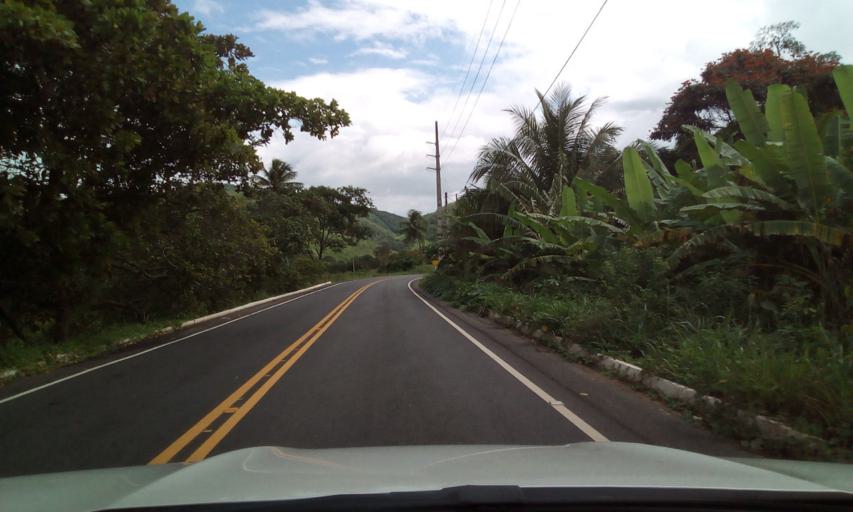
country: BR
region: Paraiba
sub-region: Alagoinha
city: Alagoinha
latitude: -6.8887
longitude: -35.5696
